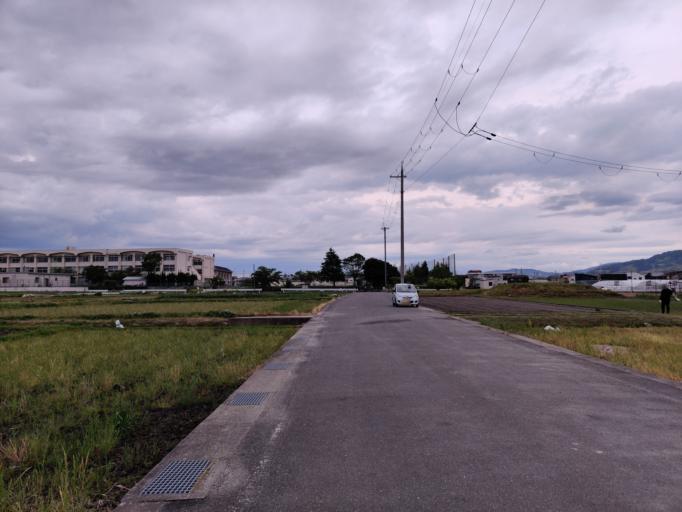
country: JP
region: Kyoto
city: Tanabe
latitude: 34.7763
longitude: 135.7936
